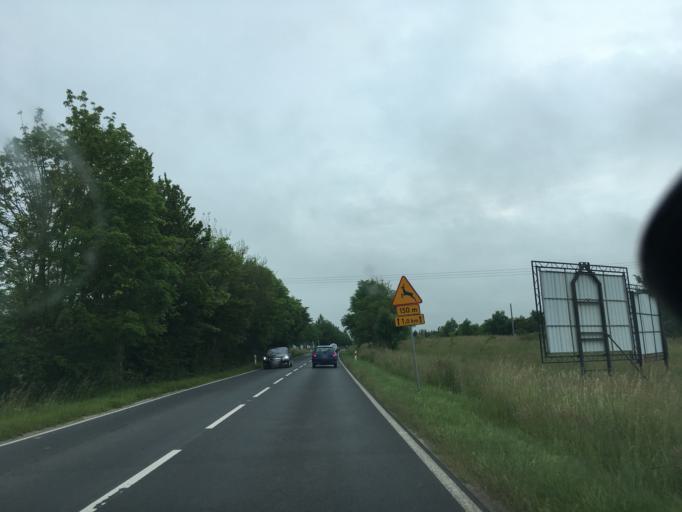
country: PL
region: West Pomeranian Voivodeship
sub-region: Powiat koszalinski
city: Mielno
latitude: 54.2502
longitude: 16.0599
